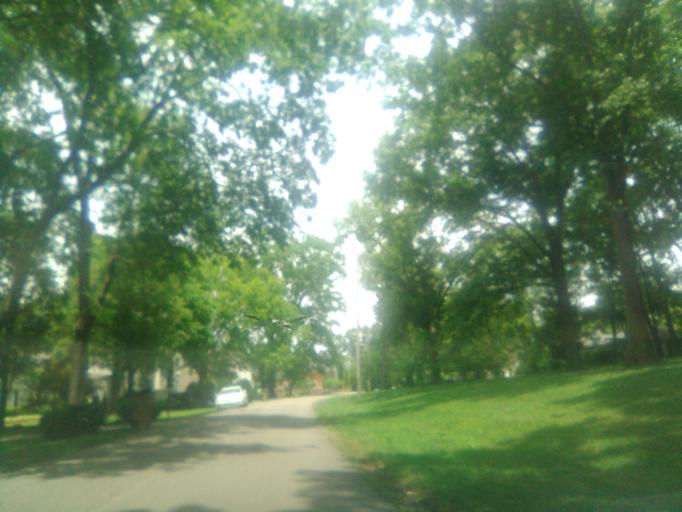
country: US
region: Tennessee
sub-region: Davidson County
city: Belle Meade
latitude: 36.0926
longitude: -86.8668
